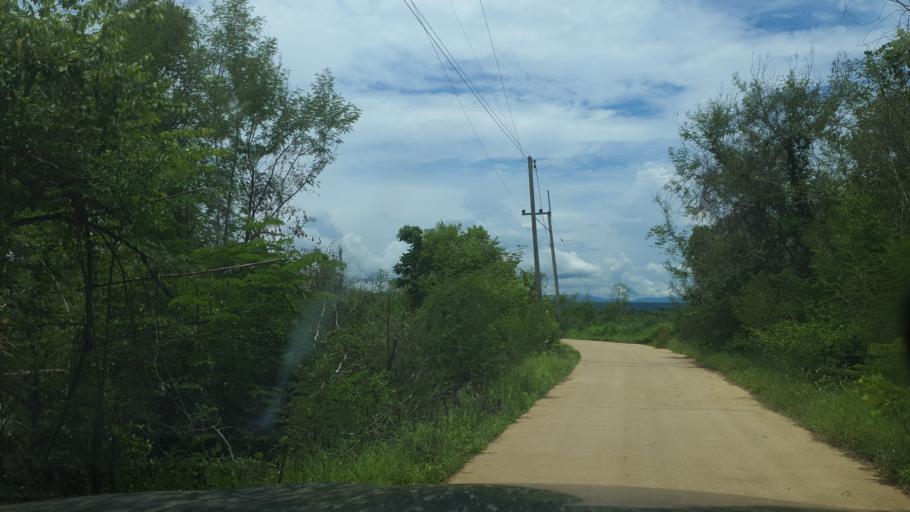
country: TH
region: Lampang
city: Ko Kha
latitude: 18.1313
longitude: 99.3354
